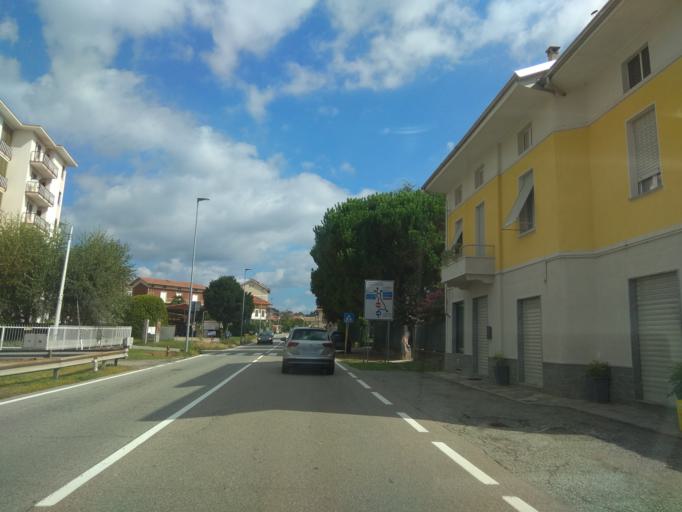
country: IT
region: Piedmont
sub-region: Provincia di Biella
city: Cossato
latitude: 45.5735
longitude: 8.1786
